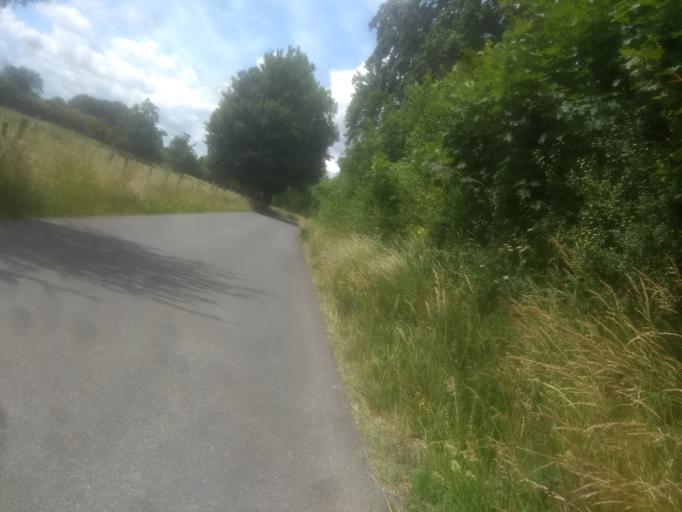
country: FR
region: Nord-Pas-de-Calais
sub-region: Departement du Pas-de-Calais
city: Maroeuil
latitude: 50.3301
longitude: 2.6917
